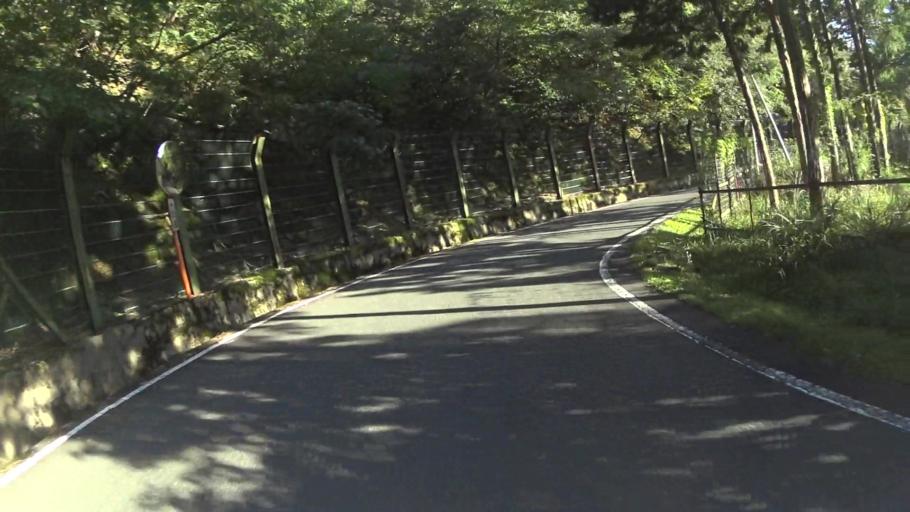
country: JP
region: Hyogo
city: Toyooka
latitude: 35.6141
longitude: 134.8777
